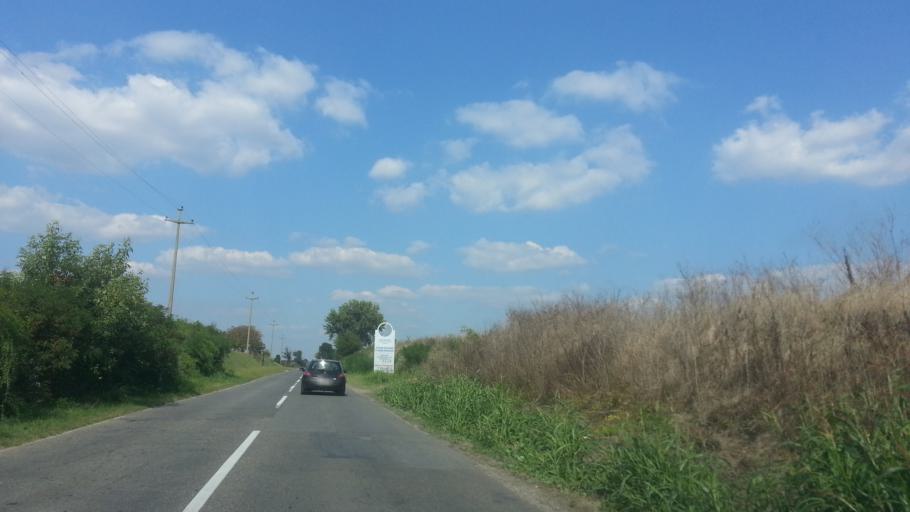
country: RS
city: Novi Banovci
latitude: 44.9319
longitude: 20.2801
